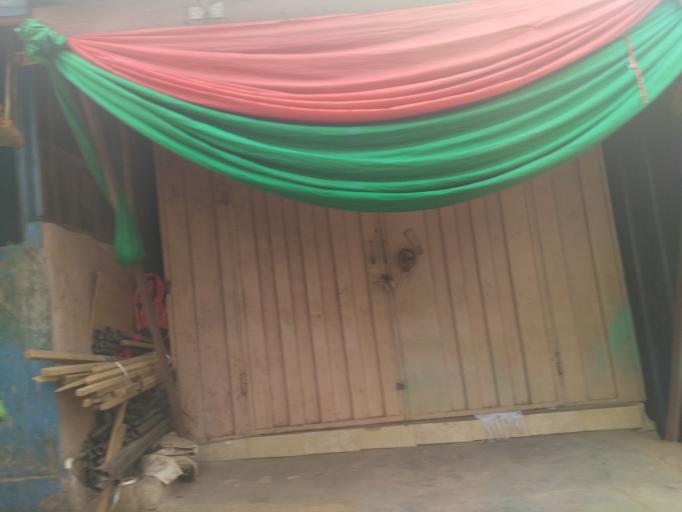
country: GH
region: Ashanti
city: Kumasi
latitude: 6.6762
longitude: -1.5921
